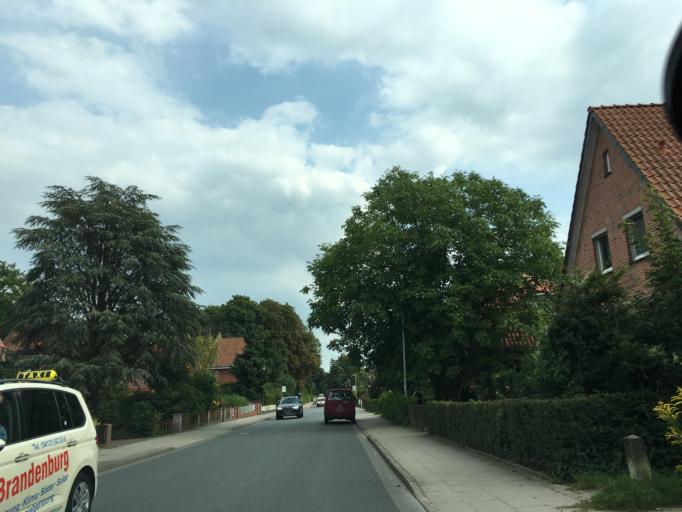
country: DE
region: Lower Saxony
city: Lueneburg
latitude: 53.2533
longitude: 10.3893
